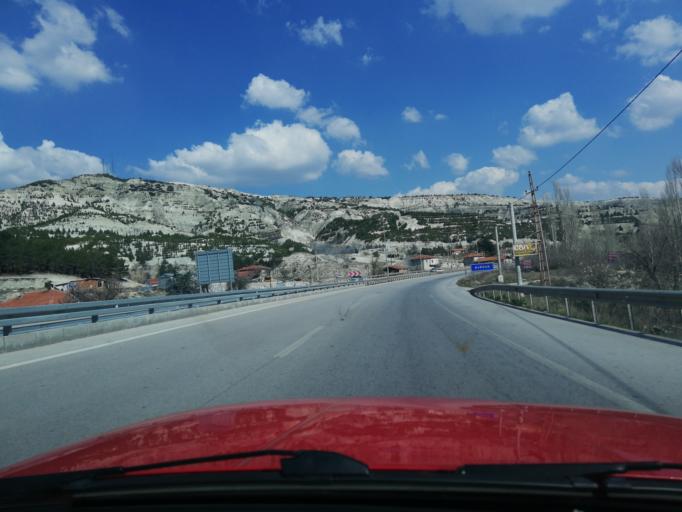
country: TR
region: Burdur
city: Burdur
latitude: 37.7090
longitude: 30.3007
